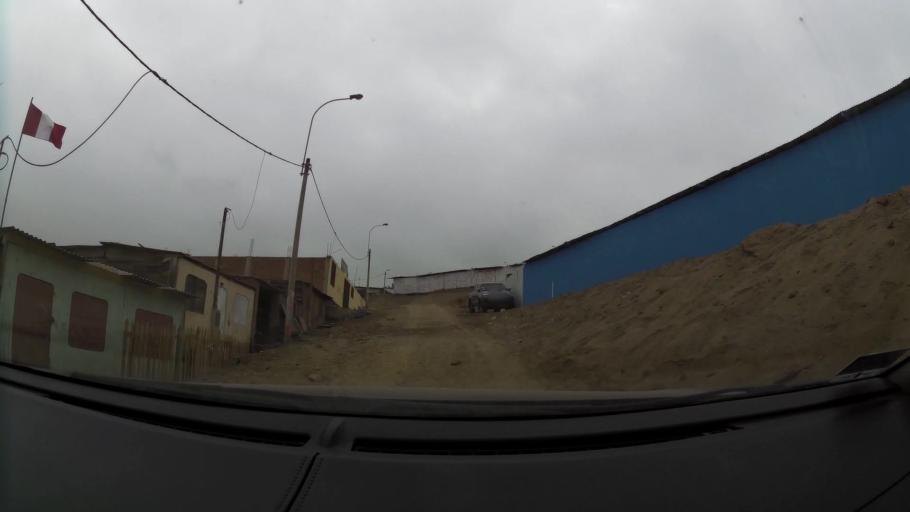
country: PE
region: Lima
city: Ventanilla
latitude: -11.8464
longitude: -77.1581
